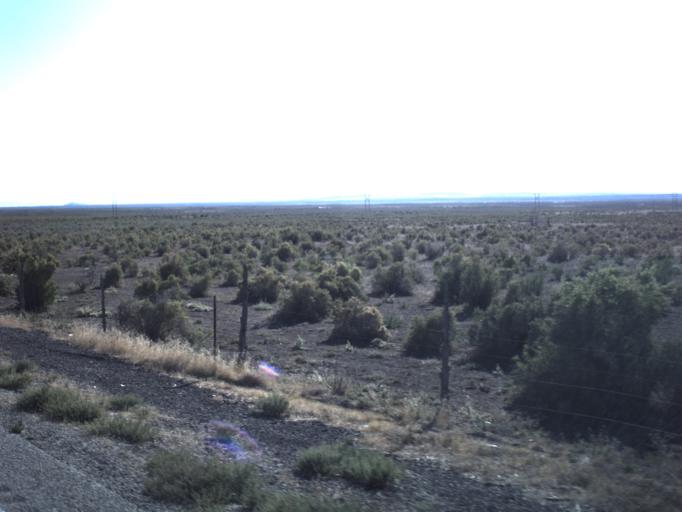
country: US
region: Utah
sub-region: Millard County
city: Fillmore
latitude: 39.1611
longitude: -112.4100
